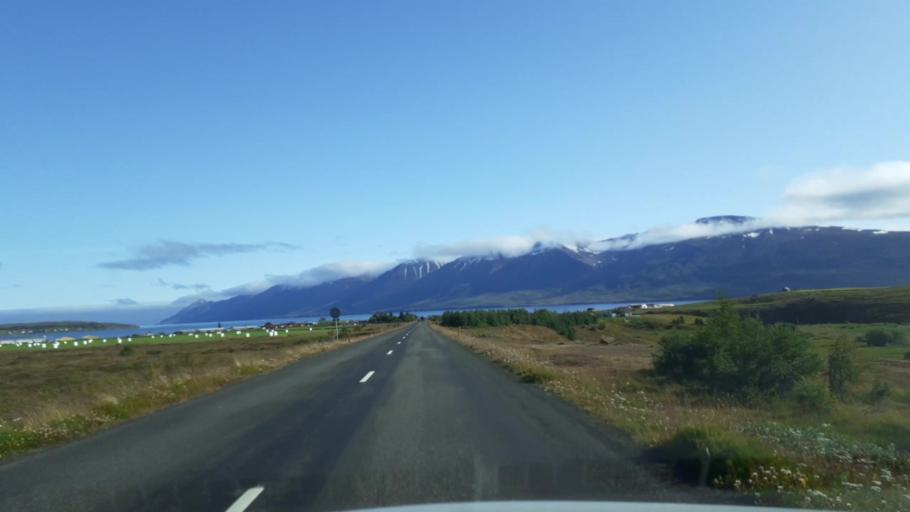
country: IS
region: Northeast
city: Dalvik
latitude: 65.9357
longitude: -18.3566
